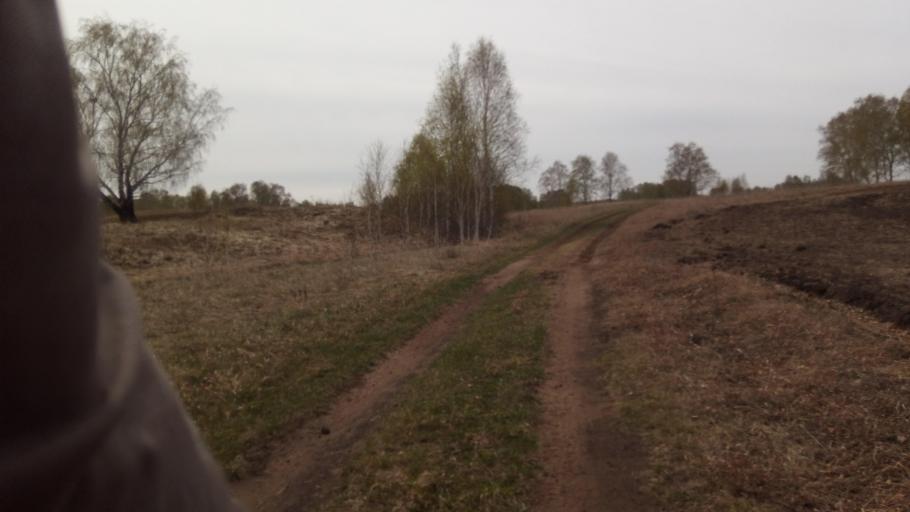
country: RU
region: Chelyabinsk
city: Timiryazevskiy
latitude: 55.0134
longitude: 60.8598
